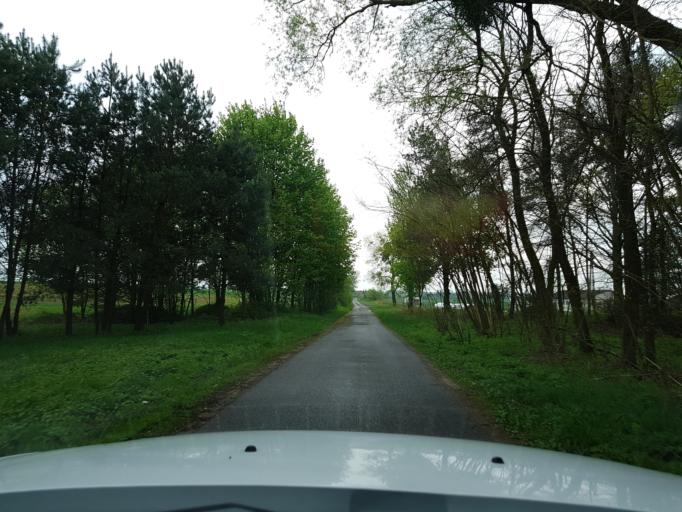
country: PL
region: West Pomeranian Voivodeship
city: Trzcinsko Zdroj
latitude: 52.9878
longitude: 14.6764
